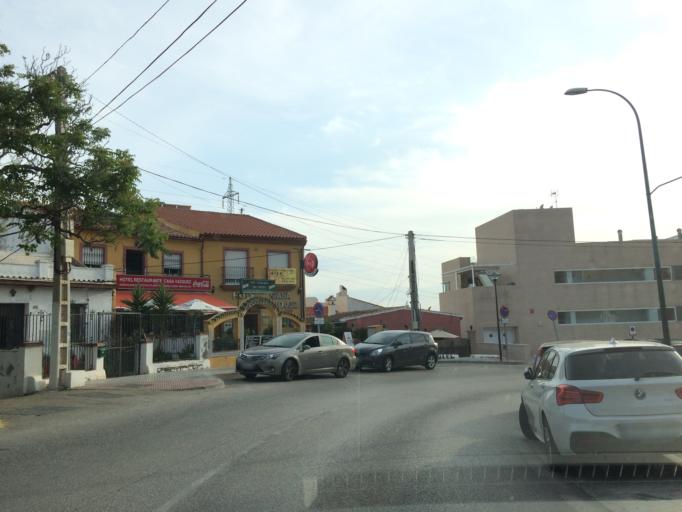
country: ES
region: Andalusia
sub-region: Provincia de Malaga
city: Malaga
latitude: 36.7365
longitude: -4.4128
